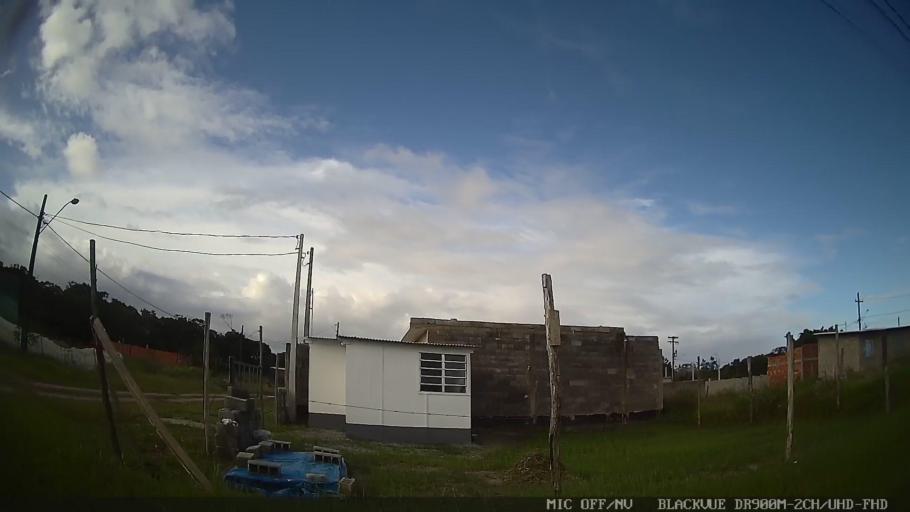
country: BR
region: Sao Paulo
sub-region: Itanhaem
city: Itanhaem
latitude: -24.2040
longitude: -46.8547
